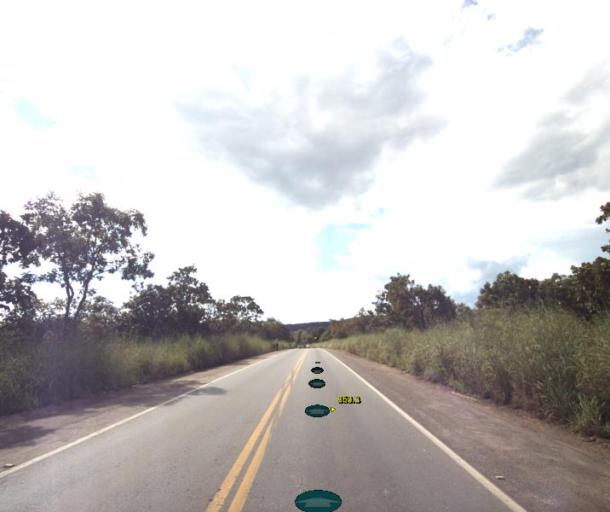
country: BR
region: Goias
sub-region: Jaragua
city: Jaragua
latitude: -15.6833
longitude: -49.3410
